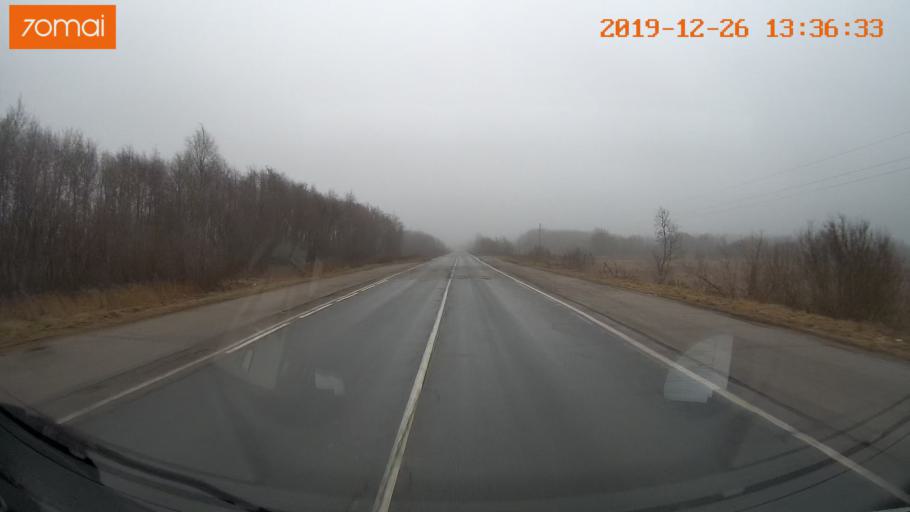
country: RU
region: Vologda
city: Sheksna
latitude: 58.7811
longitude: 38.3571
